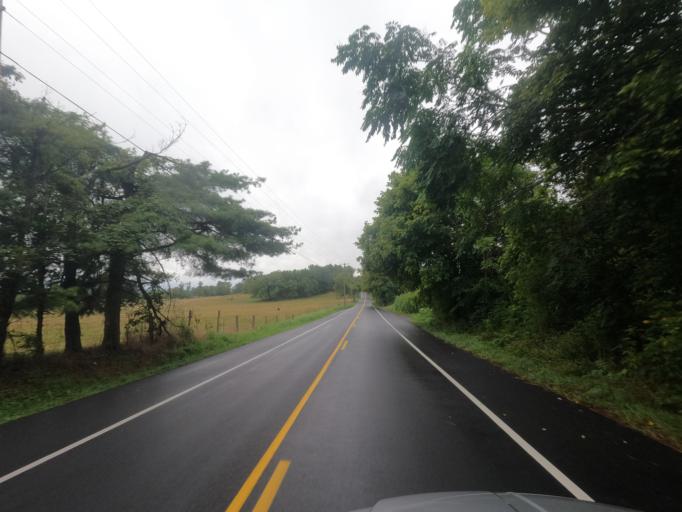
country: US
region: Maryland
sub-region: Washington County
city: Wilson-Conococheague
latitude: 39.6463
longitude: -77.9300
